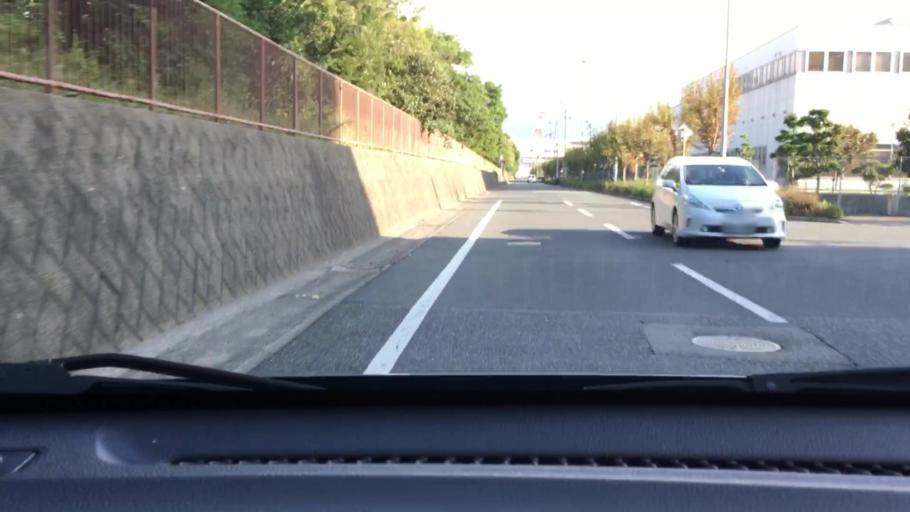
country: JP
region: Hyogo
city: Ashiya
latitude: 34.6893
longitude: 135.2757
